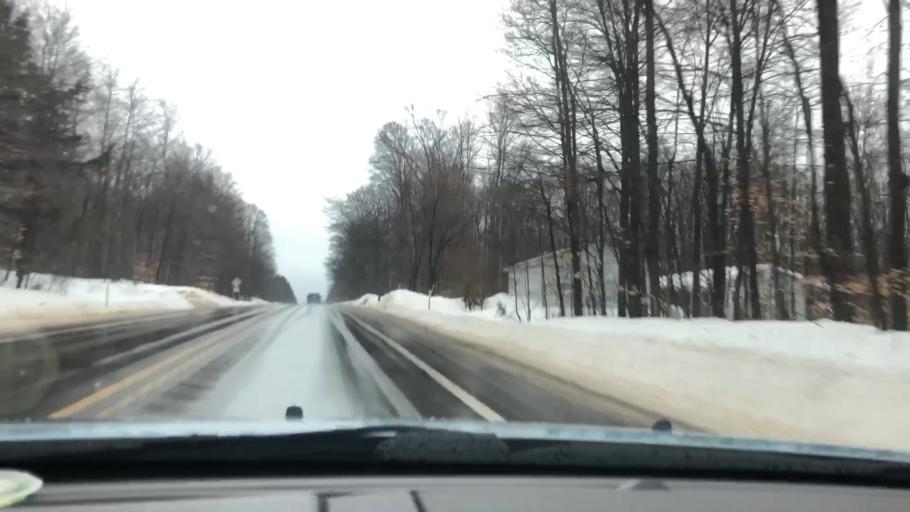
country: US
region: Michigan
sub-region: Charlevoix County
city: East Jordan
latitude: 45.1027
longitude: -85.0304
